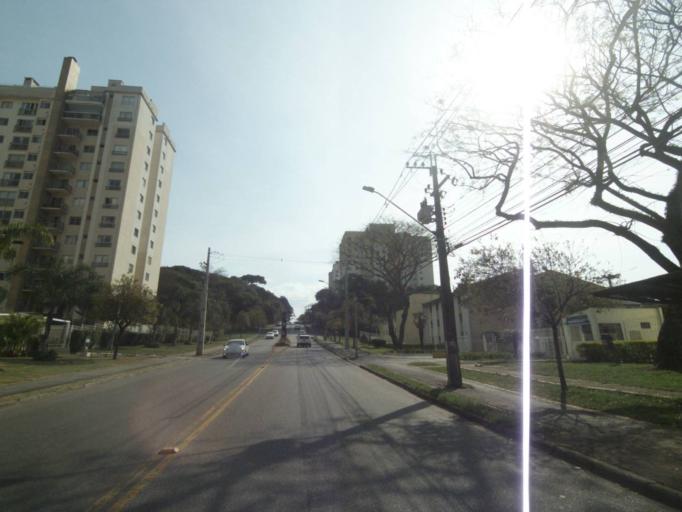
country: BR
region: Parana
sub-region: Curitiba
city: Curitiba
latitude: -25.4599
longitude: -49.3200
